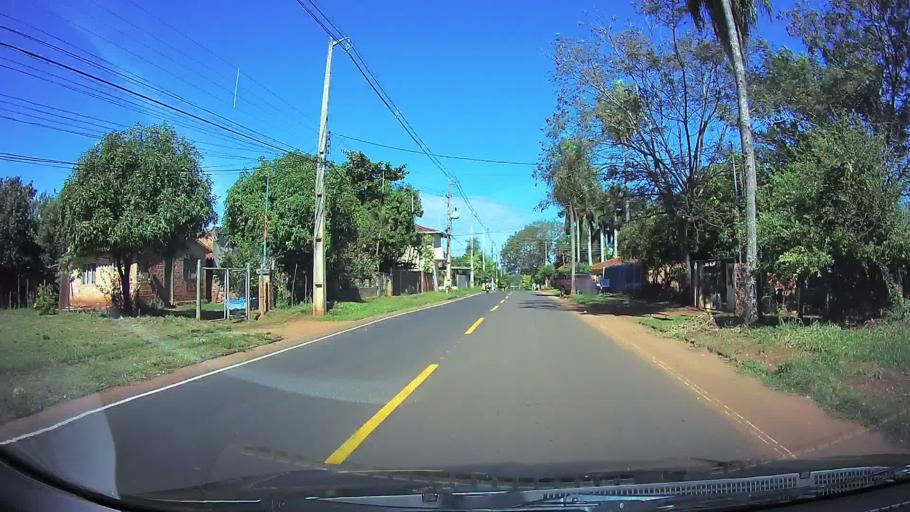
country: PY
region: Central
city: San Lorenzo
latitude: -25.2638
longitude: -57.4696
